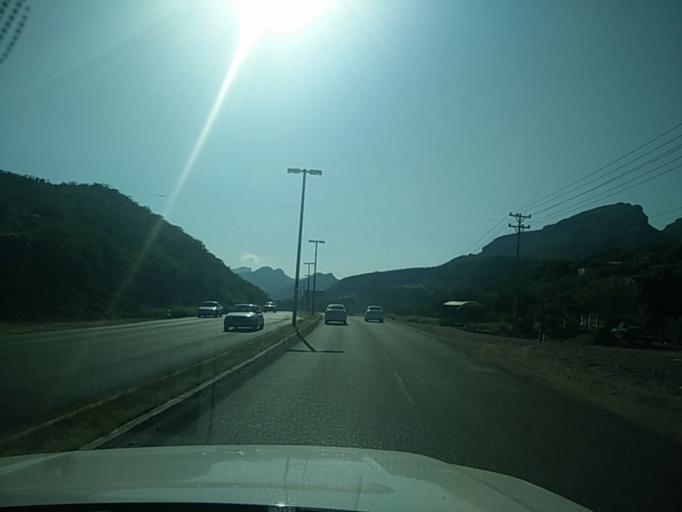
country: MX
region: Sonora
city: Heroica Guaymas
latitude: 27.9335
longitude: -110.8828
